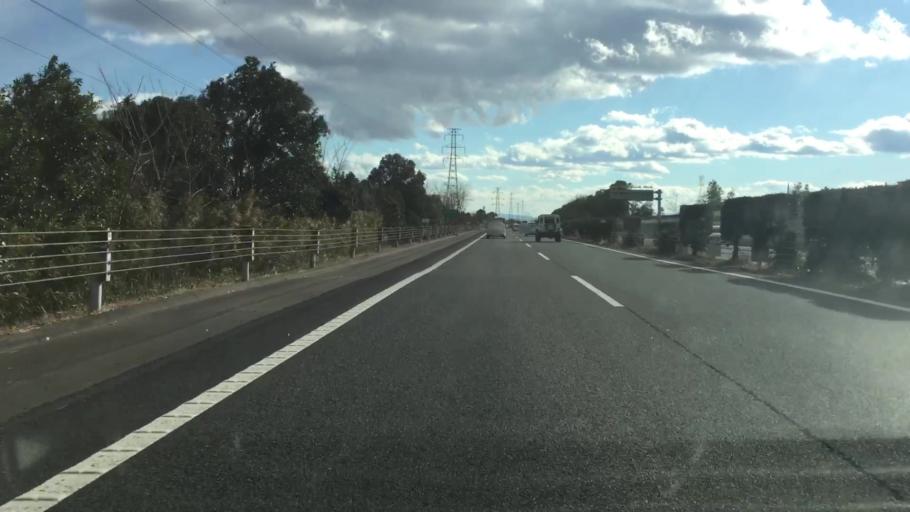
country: JP
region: Gunma
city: Shibukawa
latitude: 36.4579
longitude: 139.0130
